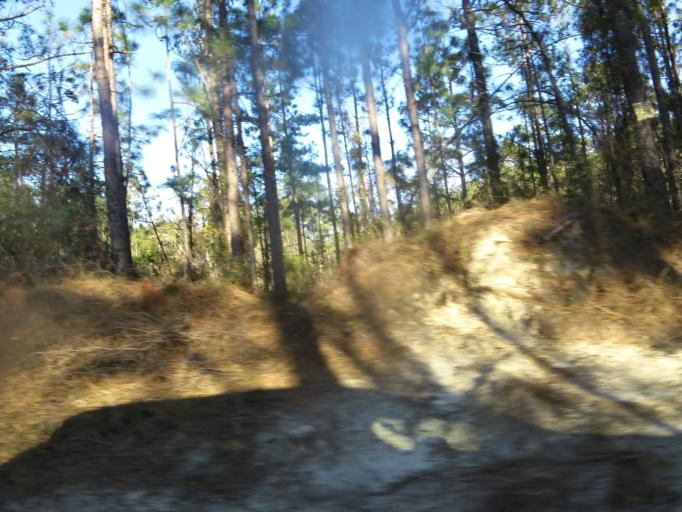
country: US
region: Florida
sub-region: Clay County
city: Middleburg
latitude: 30.1395
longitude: -81.8819
